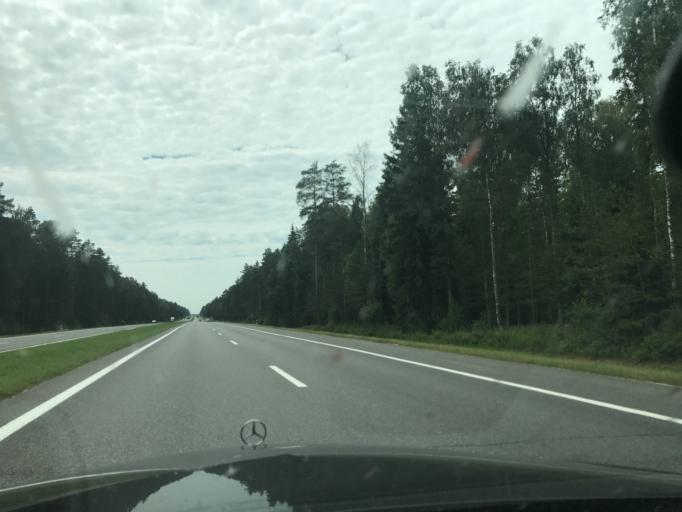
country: BY
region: Minsk
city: Slabada
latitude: 53.9215
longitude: 27.9555
